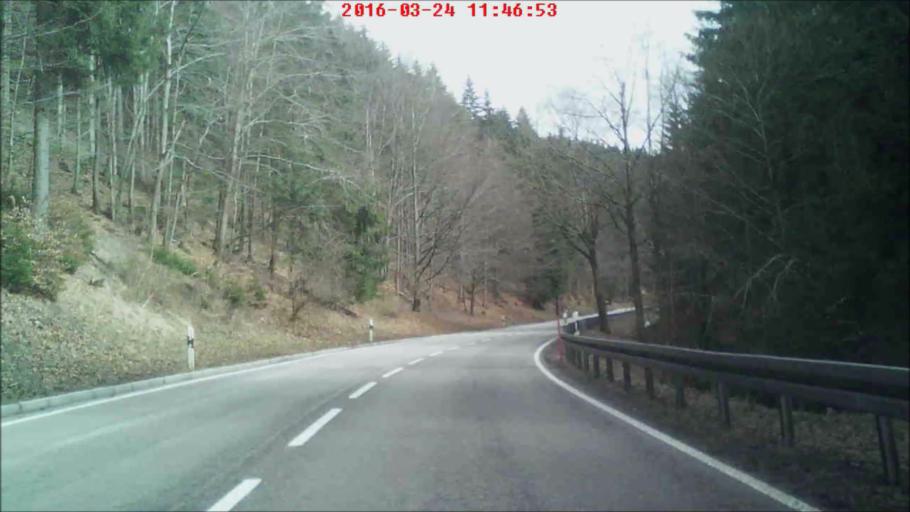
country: DE
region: Thuringia
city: Bachfeld
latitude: 50.4587
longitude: 11.0085
